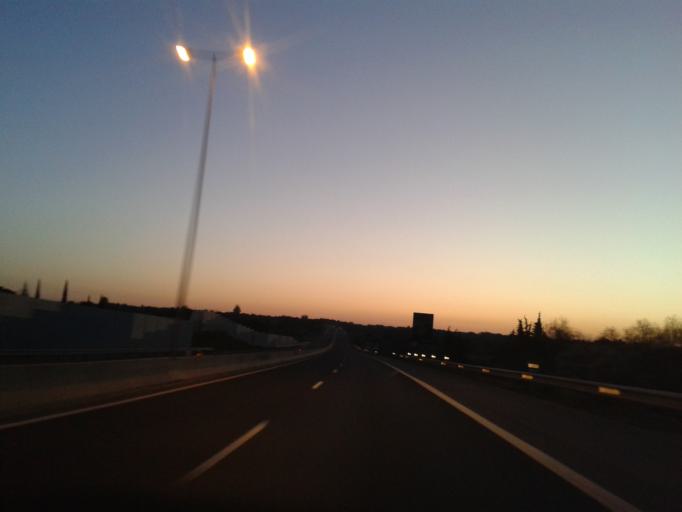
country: PT
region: Faro
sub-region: Silves
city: Armacao de Pera
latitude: 37.1356
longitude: -8.3532
